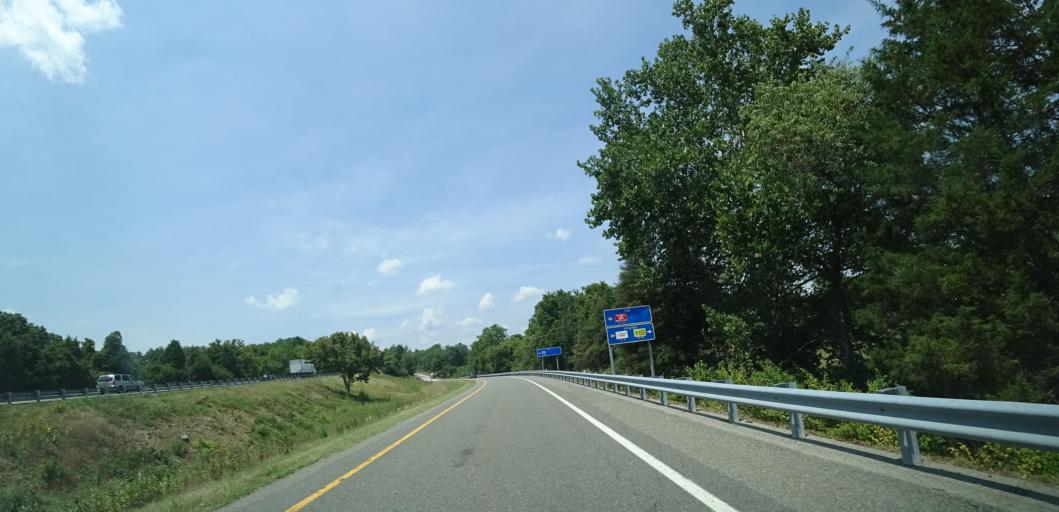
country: US
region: Virginia
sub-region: Botetourt County
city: Fincastle
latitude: 37.4583
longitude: -79.8374
